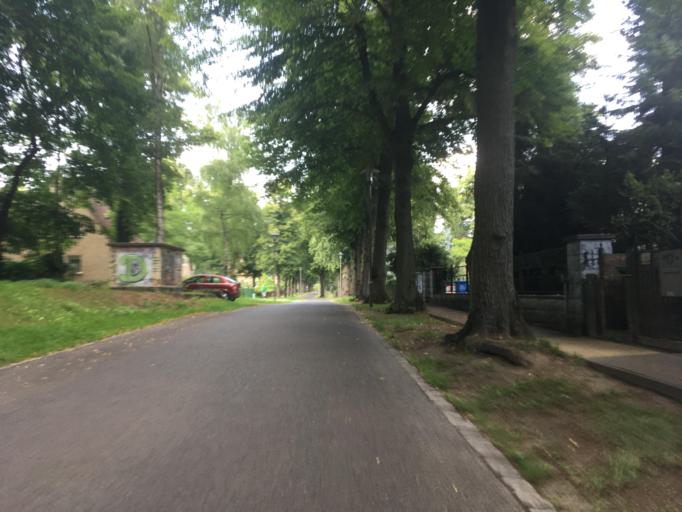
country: DE
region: Brandenburg
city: Zeuthen
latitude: 52.3438
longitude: 13.6269
